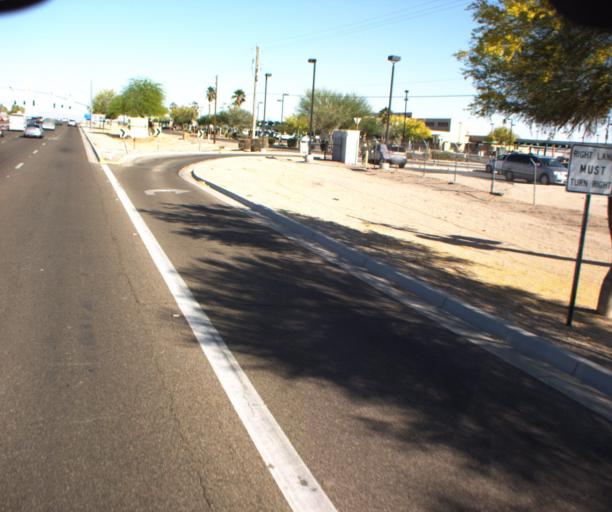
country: US
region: Arizona
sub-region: Yuma County
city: Yuma
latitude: 32.6693
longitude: -114.6014
